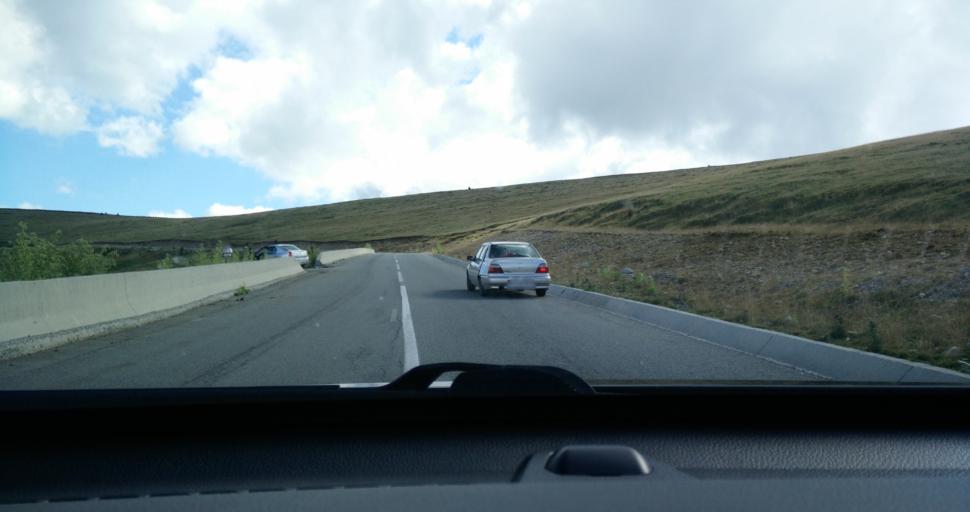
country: RO
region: Gorj
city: Novaci-Straini
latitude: 45.2519
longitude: 23.6952
